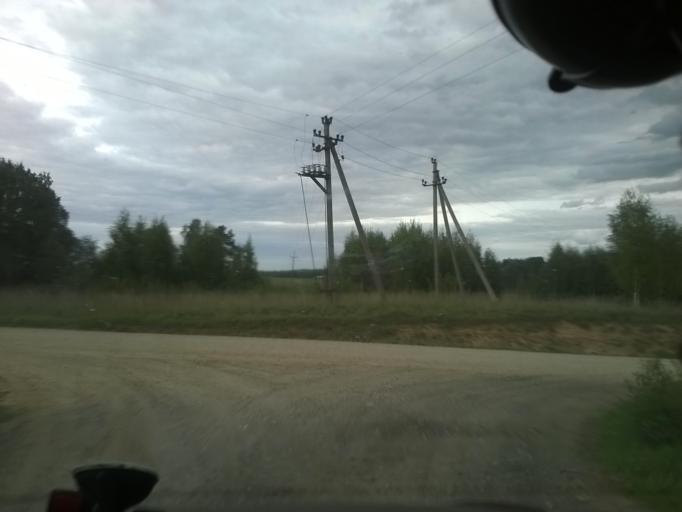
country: EE
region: Vorumaa
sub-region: Voru linn
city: Voru
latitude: 57.8109
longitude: 27.1683
